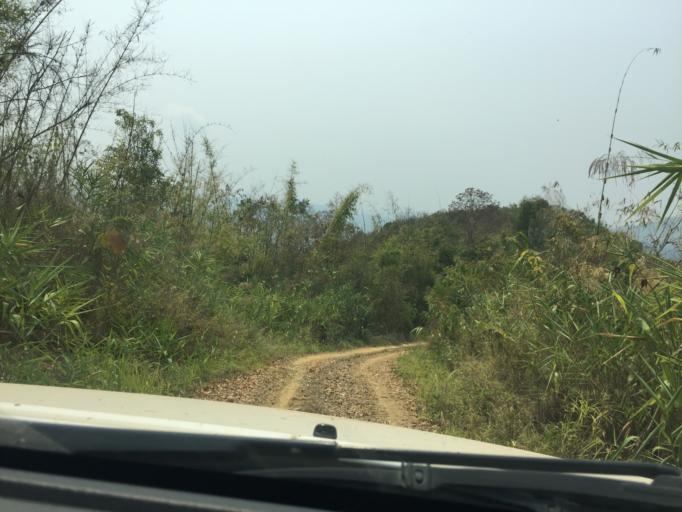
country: LA
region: Loungnamtha
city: Muang Nale
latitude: 20.6145
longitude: 101.6044
